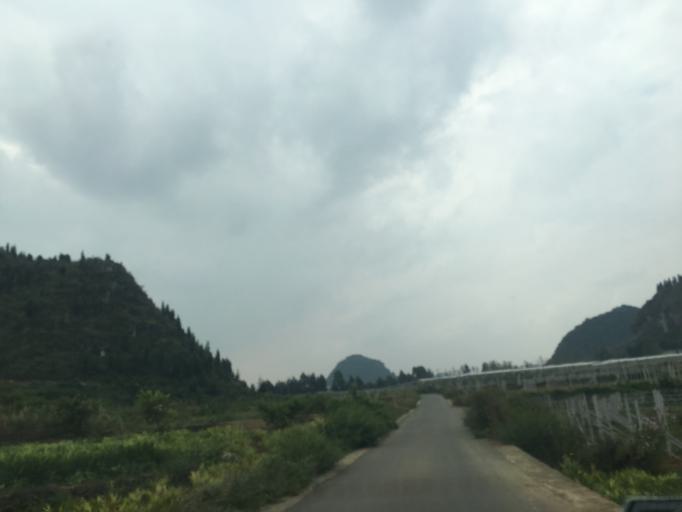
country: CN
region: Guangxi Zhuangzu Zizhiqu
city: Xinzhou
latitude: 25.4831
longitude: 105.6476
